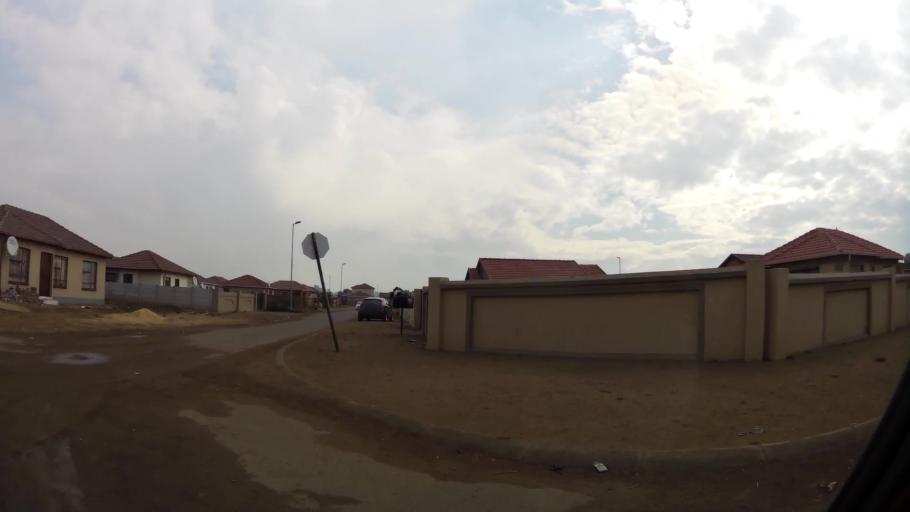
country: ZA
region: Gauteng
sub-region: Sedibeng District Municipality
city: Vanderbijlpark
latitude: -26.6840
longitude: 27.8455
